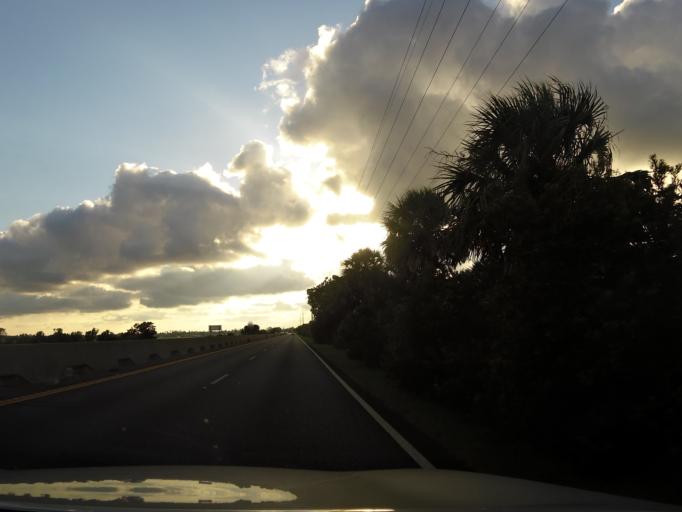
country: US
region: Georgia
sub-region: Glynn County
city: Brunswick
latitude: 31.1623
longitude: -81.4612
